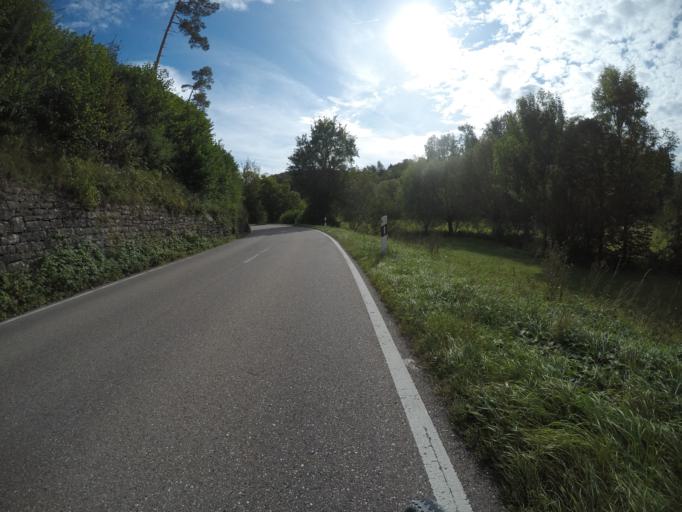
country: DE
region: Baden-Wuerttemberg
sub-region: Regierungsbezirk Stuttgart
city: Eberdingen
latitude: 48.8556
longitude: 8.9594
